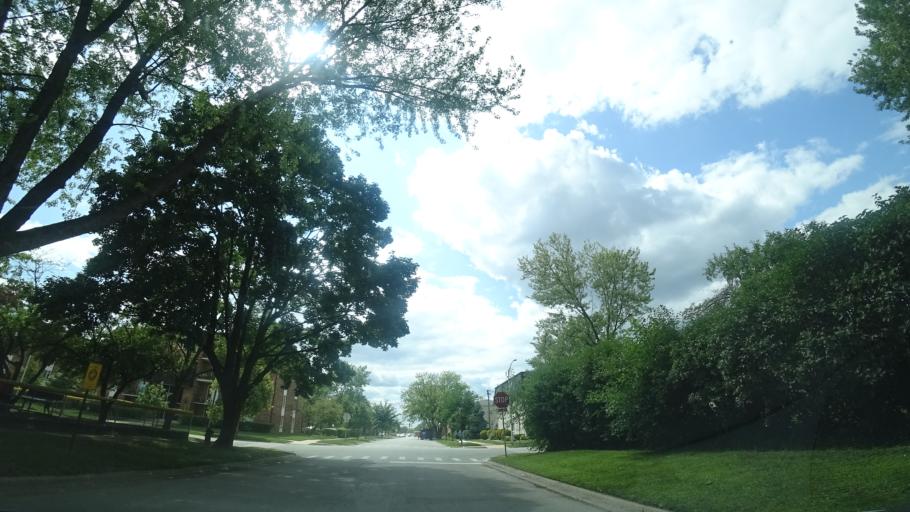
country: US
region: Illinois
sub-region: Cook County
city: Alsip
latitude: 41.6928
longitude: -87.7369
